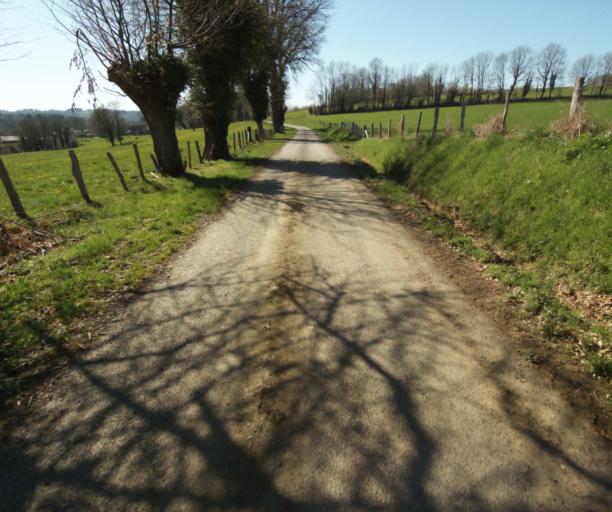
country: FR
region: Limousin
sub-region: Departement de la Correze
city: Chamboulive
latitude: 45.4147
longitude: 1.6364
